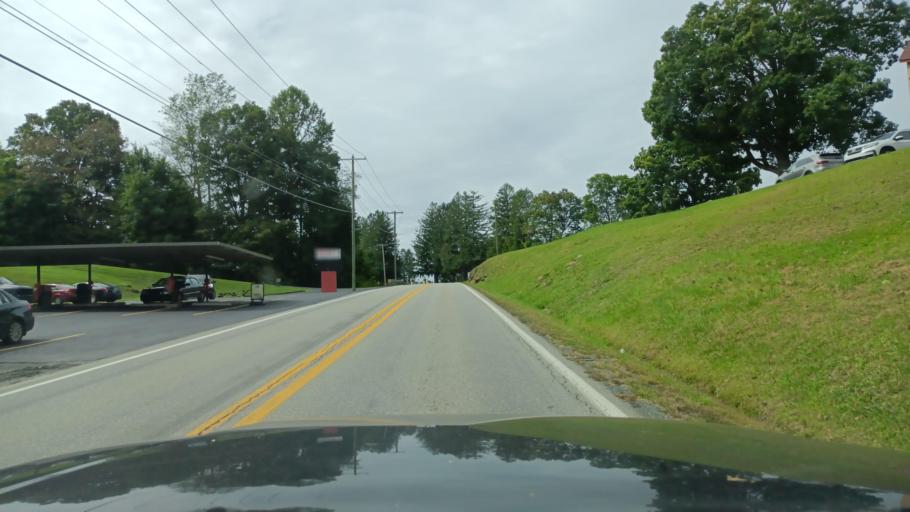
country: US
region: West Virginia
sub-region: Taylor County
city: Grafton
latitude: 39.3485
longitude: -80.0135
